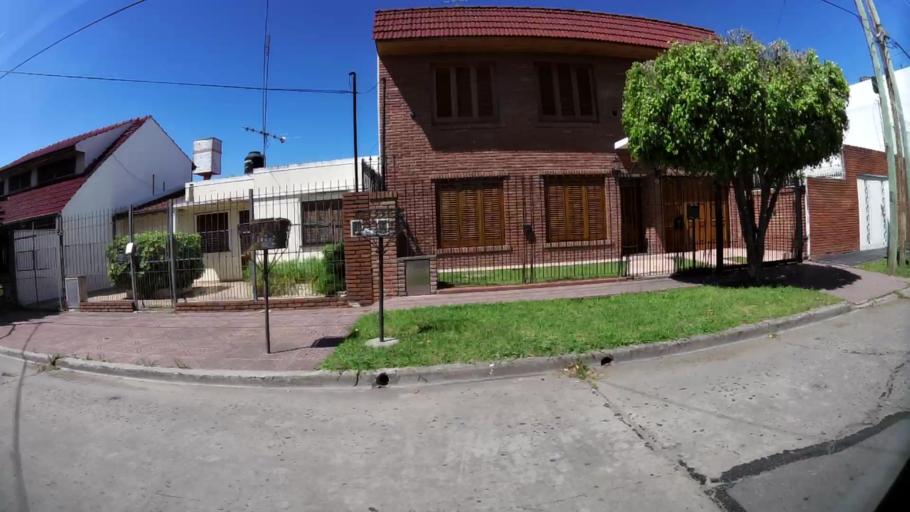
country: AR
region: Buenos Aires
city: Ituzaingo
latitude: -34.6636
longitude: -58.6519
